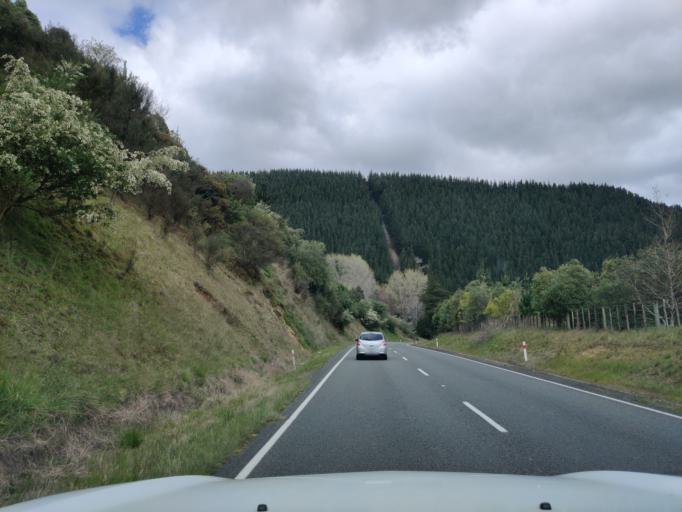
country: NZ
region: Manawatu-Wanganui
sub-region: Wanganui District
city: Wanganui
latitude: -39.8099
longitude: 175.1893
